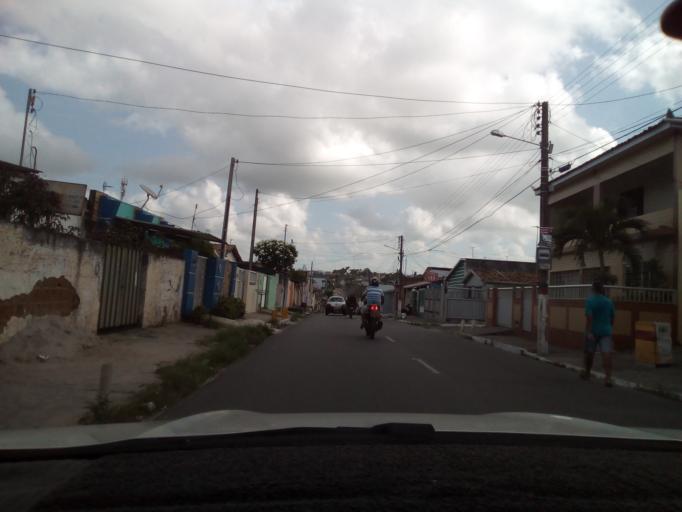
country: BR
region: Paraiba
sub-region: Bayeux
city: Bayeux
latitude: -7.1269
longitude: -34.9310
